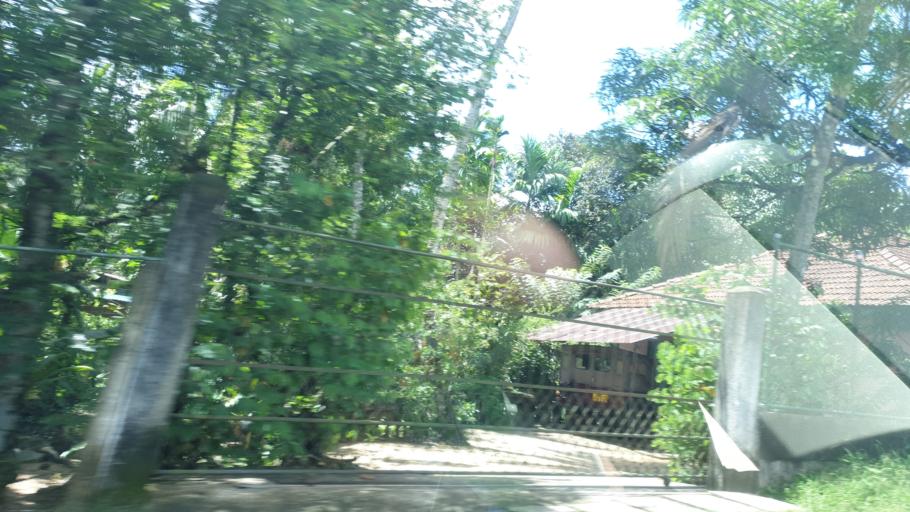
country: LK
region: Western
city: Horawala Junction
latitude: 6.5216
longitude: 80.2196
